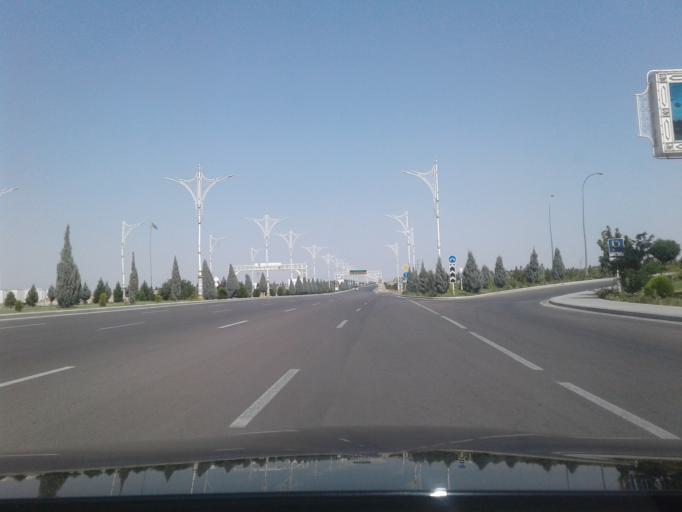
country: TM
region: Ahal
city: Ashgabat
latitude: 37.8786
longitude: 58.3926
